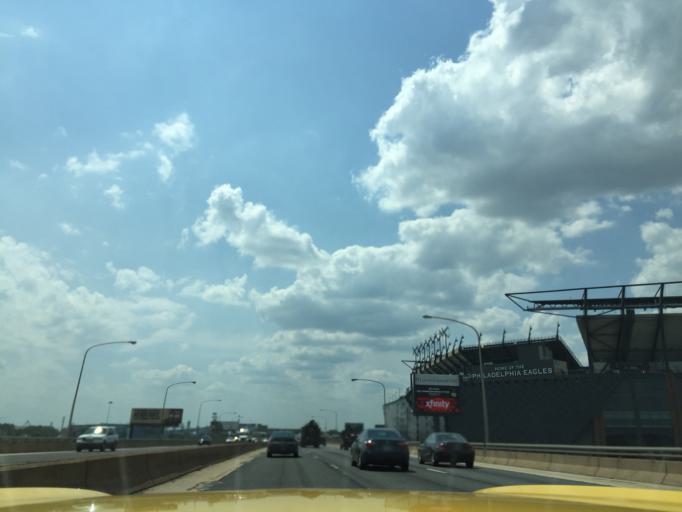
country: US
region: New Jersey
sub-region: Gloucester County
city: National Park
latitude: 39.8995
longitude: -75.1641
